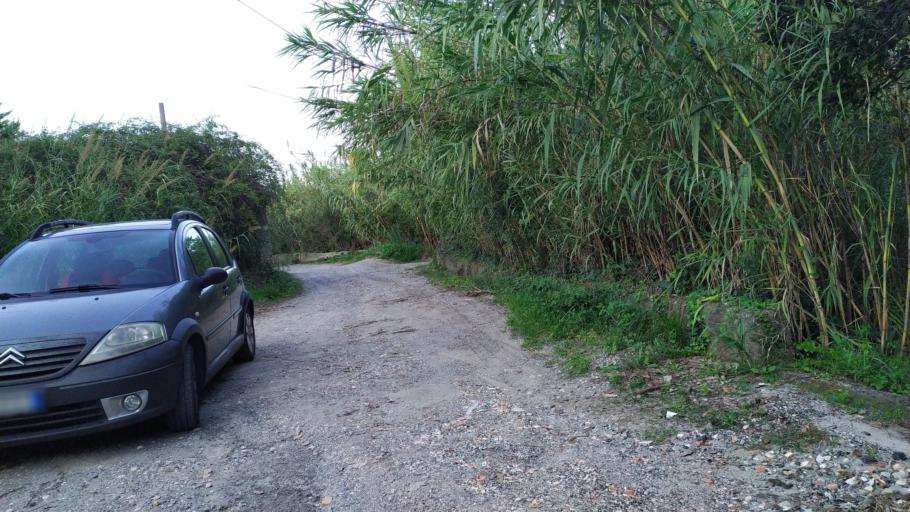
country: IT
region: Sicily
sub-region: Messina
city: Saponara Marittima
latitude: 38.2282
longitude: 15.4361
